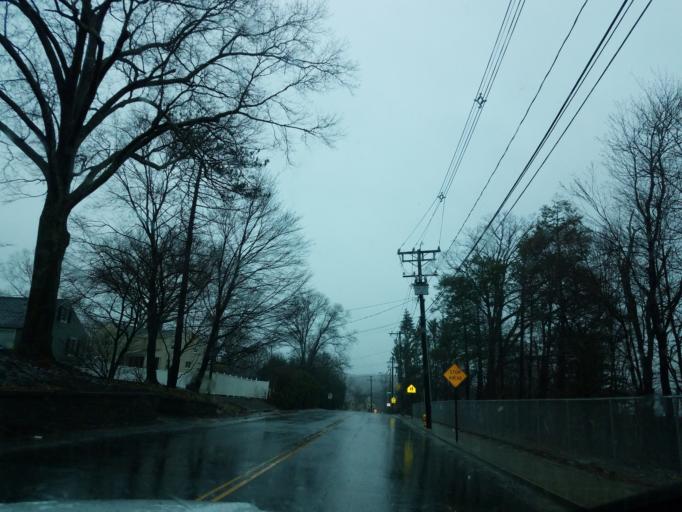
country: US
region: Connecticut
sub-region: New Haven County
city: Waterbury
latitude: 41.5451
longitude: -73.0678
